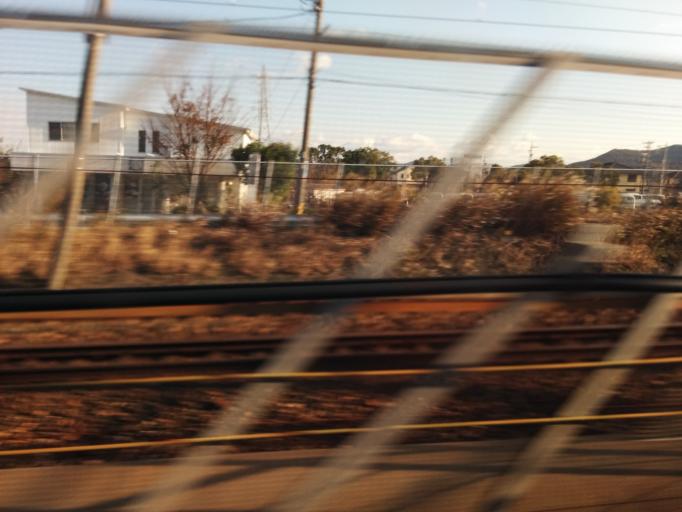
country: JP
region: Aichi
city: Toyohashi
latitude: 34.7322
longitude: 137.4157
